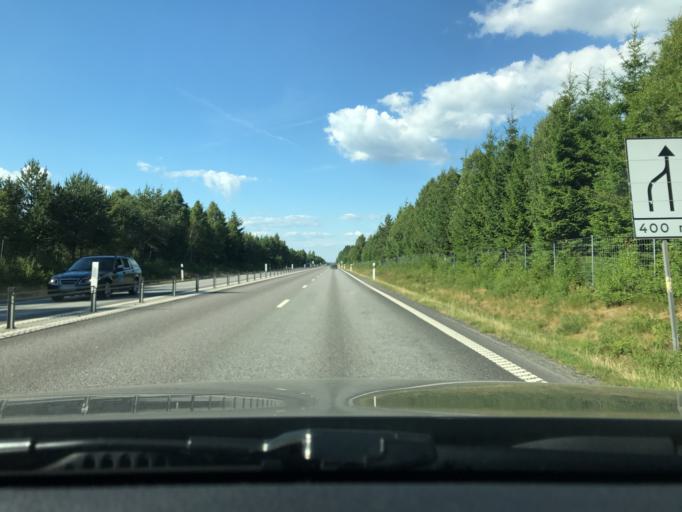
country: SE
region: Kronoberg
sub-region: Almhults Kommun
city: AElmhult
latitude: 56.4826
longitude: 14.1121
